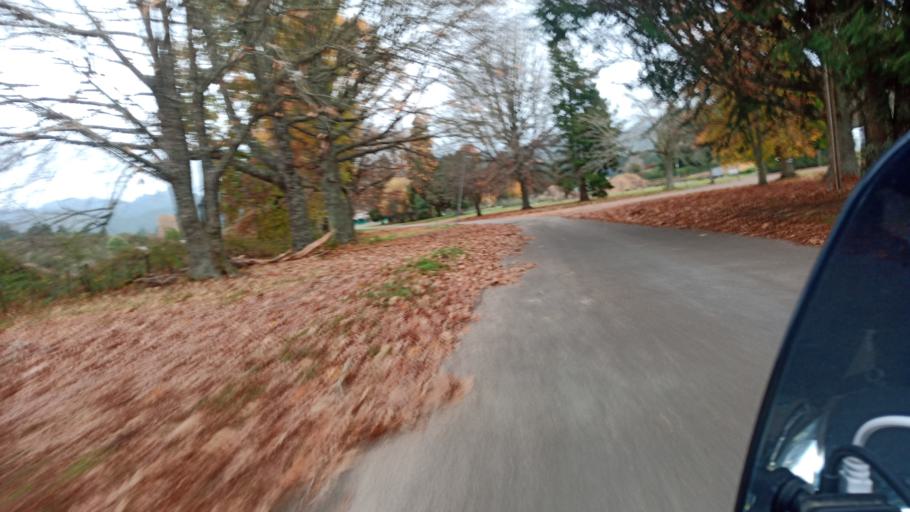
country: NZ
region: Bay of Plenty
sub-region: Whakatane District
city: Murupara
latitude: -38.6408
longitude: 176.7275
